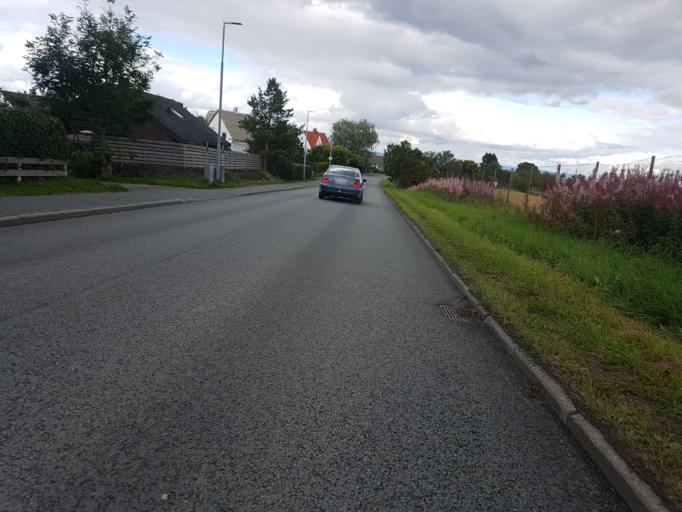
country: NO
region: Sor-Trondelag
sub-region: Trondheim
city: Trondheim
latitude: 63.4204
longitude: 10.4488
